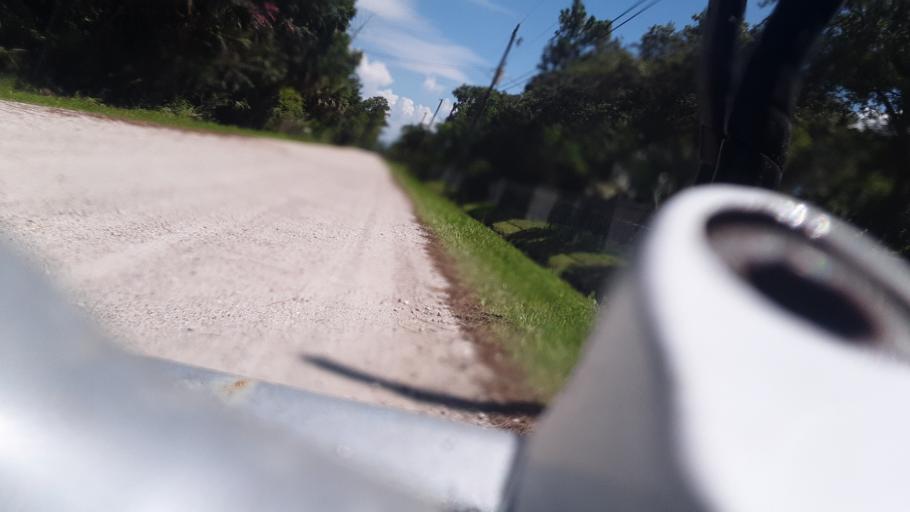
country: US
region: Florida
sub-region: Brevard County
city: Malabar
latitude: 27.9893
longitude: -80.5978
